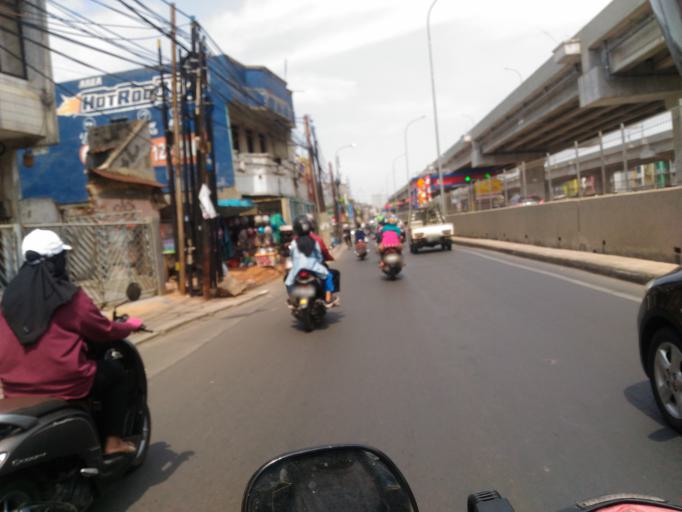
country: ID
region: West Java
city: Bekasi
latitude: -6.2497
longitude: 106.9492
